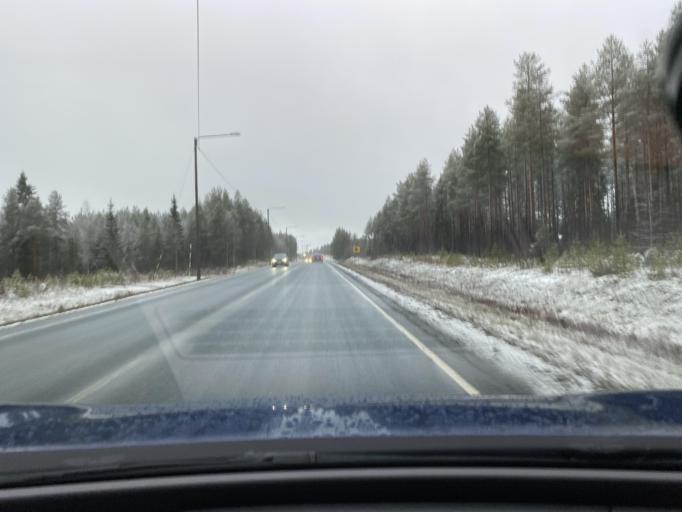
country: FI
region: Northern Ostrobothnia
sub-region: Oulu
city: Kiiminki
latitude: 65.1258
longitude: 25.7651
